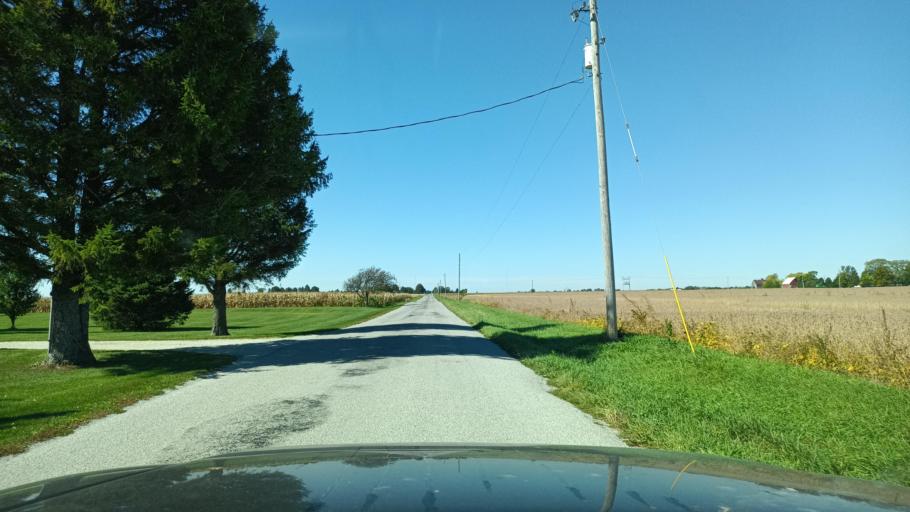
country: US
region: Illinois
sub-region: Champaign County
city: Mahomet
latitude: 40.0988
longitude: -88.3635
